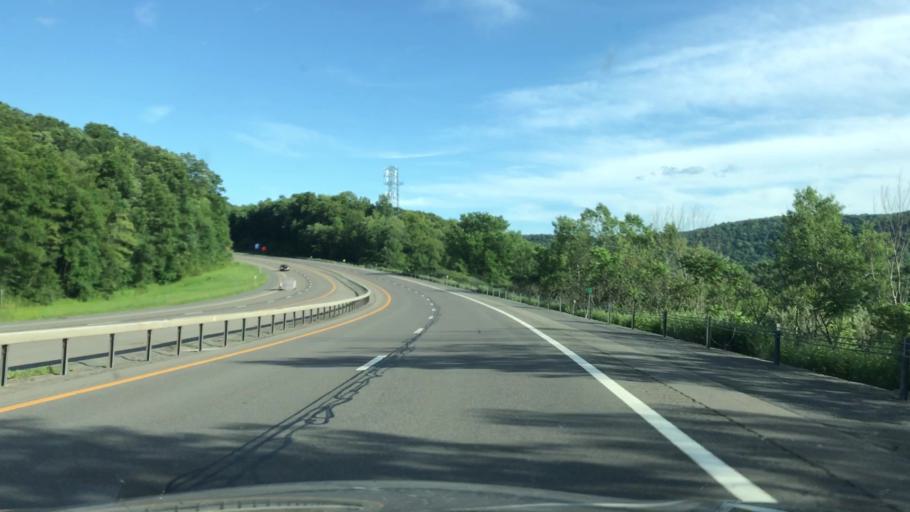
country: US
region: New York
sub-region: Delaware County
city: Hancock
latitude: 41.9574
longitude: -75.3152
